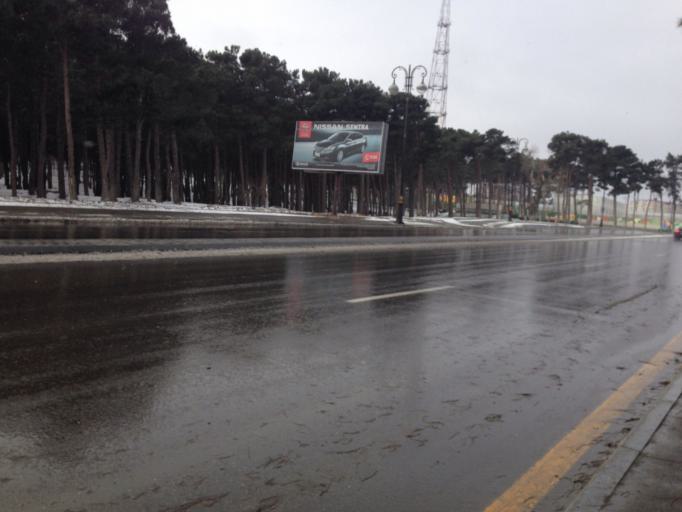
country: AZ
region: Baki
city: Baku
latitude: 40.3958
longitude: 49.8517
